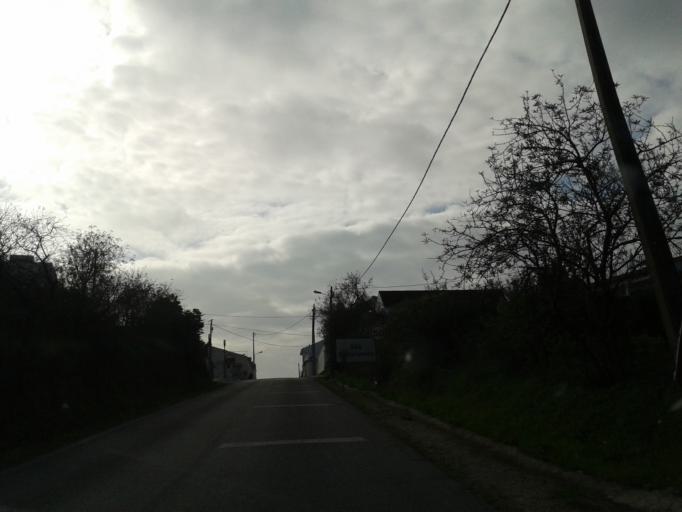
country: PT
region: Faro
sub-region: Vila Real de Santo Antonio
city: Monte Gordo
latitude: 37.1948
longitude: -7.4846
